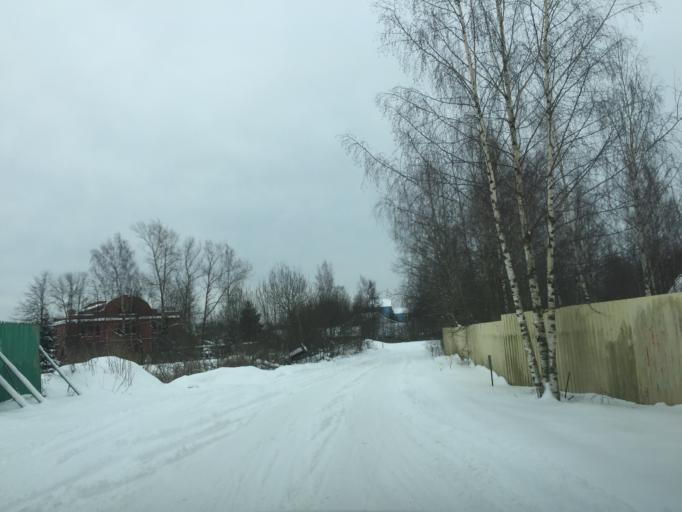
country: RU
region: Leningrad
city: Otradnoye
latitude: 59.7878
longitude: 30.7885
